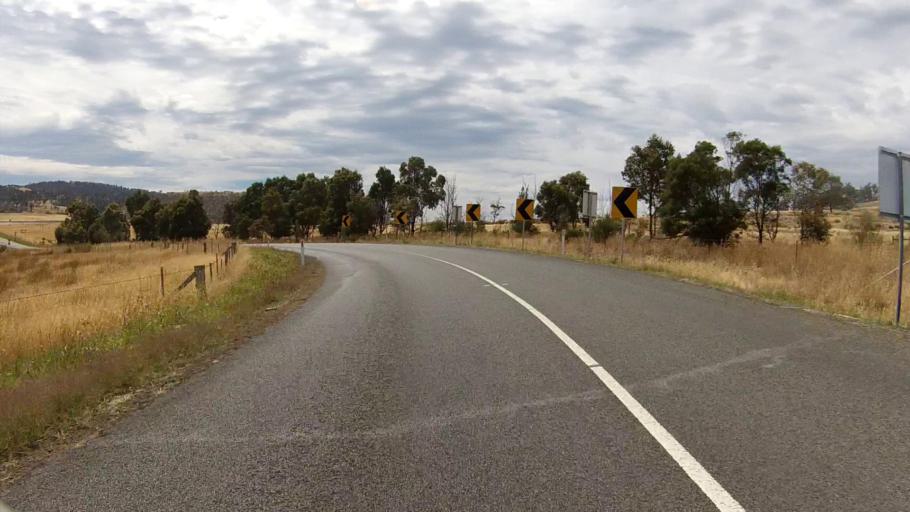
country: AU
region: Tasmania
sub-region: Sorell
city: Sorell
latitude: -42.8737
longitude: 147.6821
